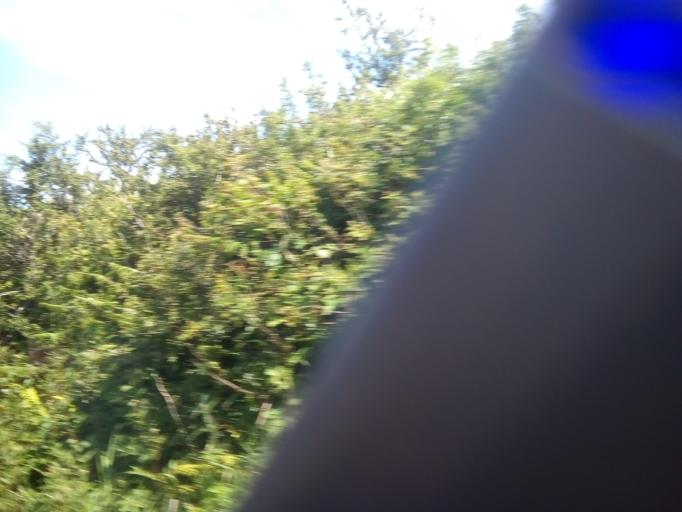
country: IE
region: Leinster
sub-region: Loch Garman
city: Loch Garman
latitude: 52.2417
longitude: -6.6027
